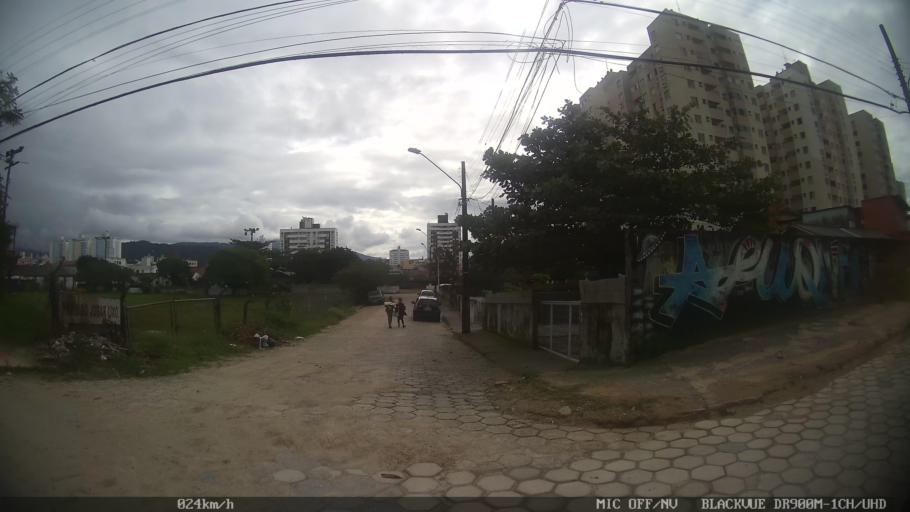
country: BR
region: Santa Catarina
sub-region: Sao Jose
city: Campinas
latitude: -27.5585
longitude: -48.6250
